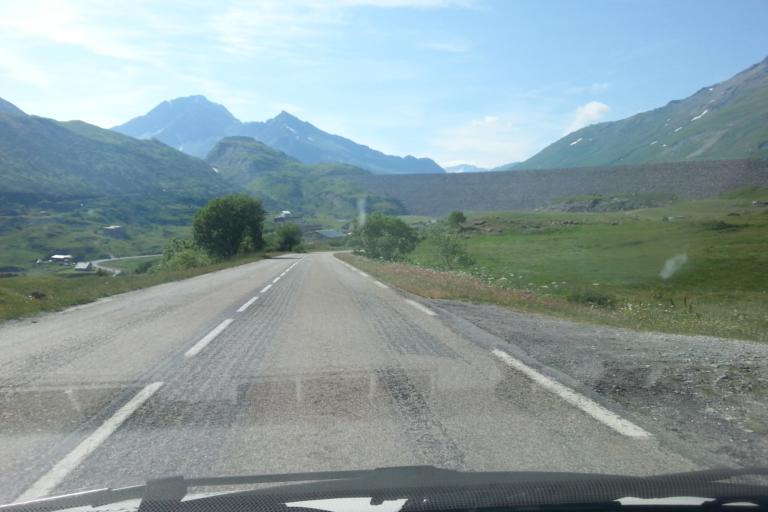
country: IT
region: Piedmont
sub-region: Provincia di Torino
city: Moncenisio
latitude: 45.2156
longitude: 6.9625
